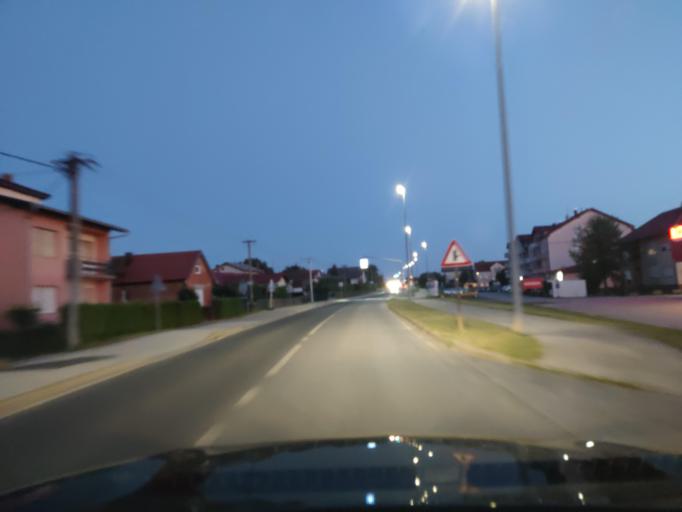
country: HR
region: Medimurska
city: Vratisinec
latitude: 46.5074
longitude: 16.4320
